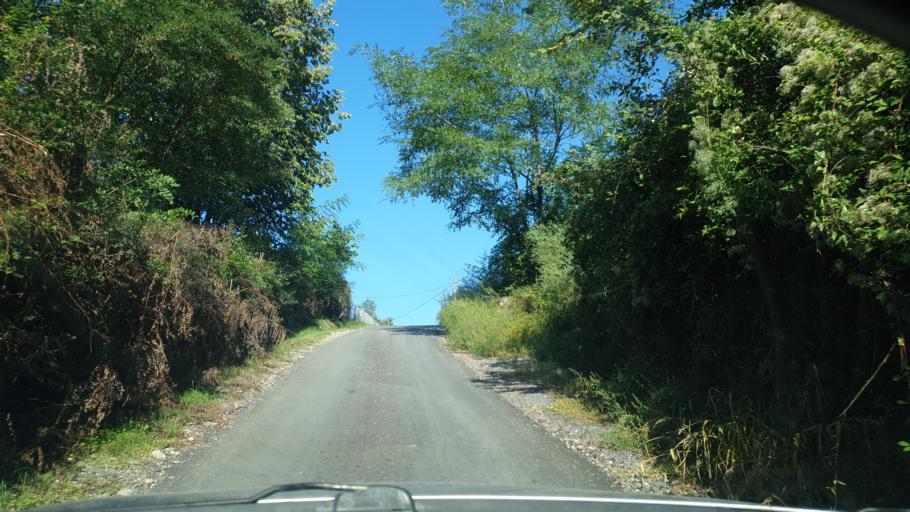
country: RS
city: Jarebice
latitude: 44.5033
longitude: 19.4856
